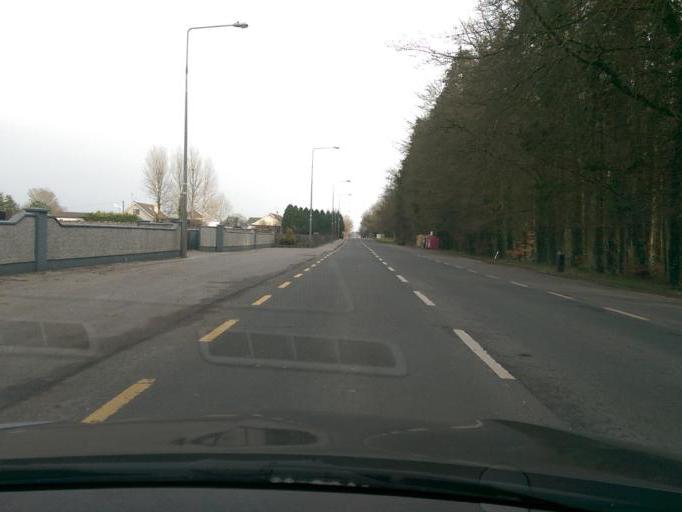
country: IE
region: Connaught
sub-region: County Galway
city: Loughrea
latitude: 53.4735
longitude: -8.5161
